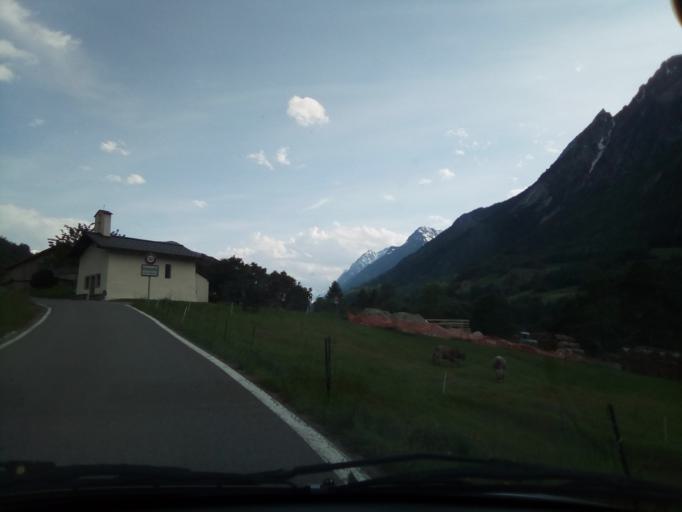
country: CH
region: Valais
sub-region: Entremont District
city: Orsieres
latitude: 46.0613
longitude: 7.1527
